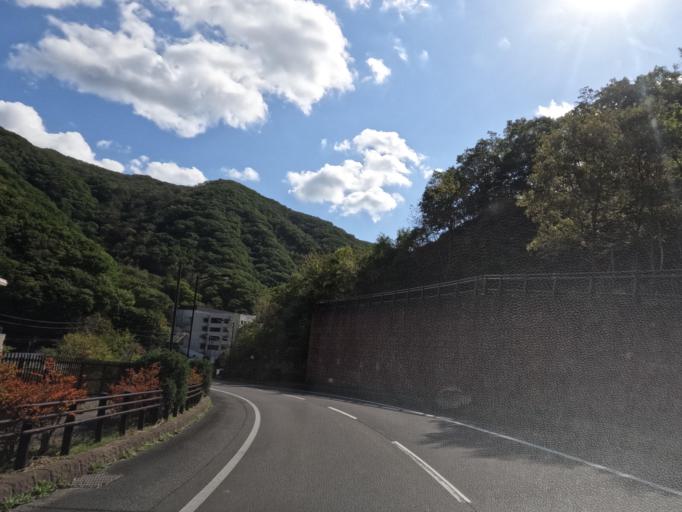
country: JP
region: Hokkaido
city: Shiraoi
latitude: 42.4893
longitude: 141.1456
